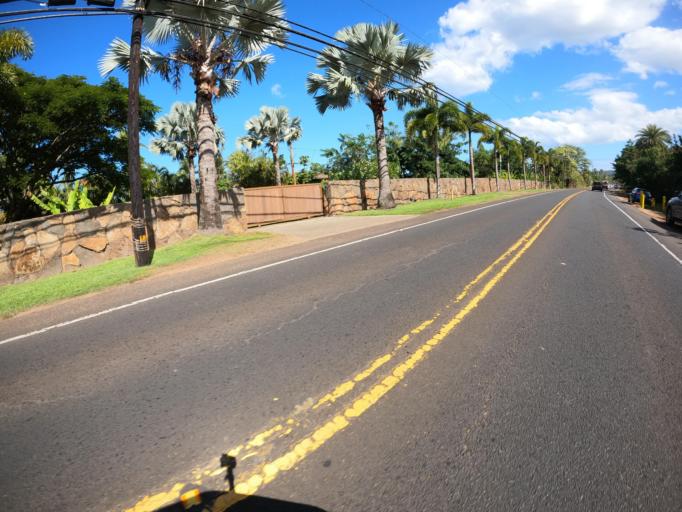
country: US
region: Hawaii
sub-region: Honolulu County
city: Hale'iwa
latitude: 21.6198
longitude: -158.0840
